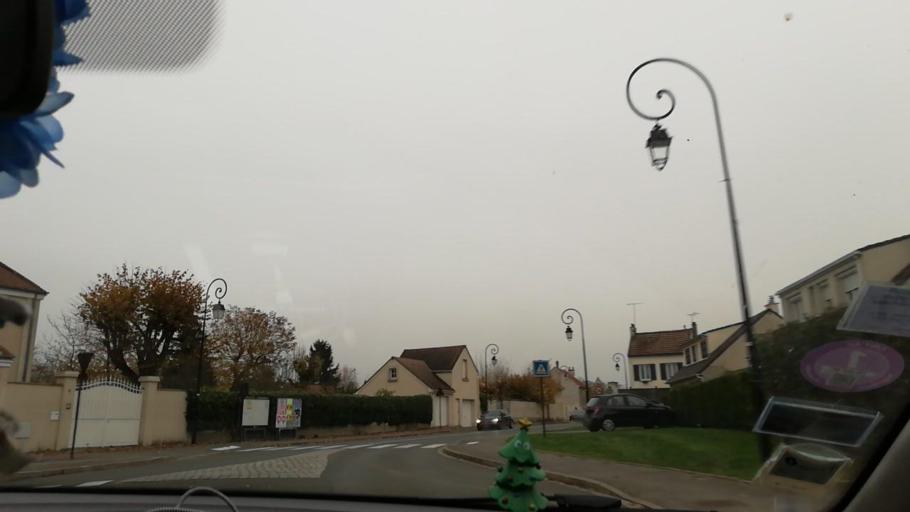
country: FR
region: Ile-de-France
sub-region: Departement de Seine-et-Marne
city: Claye-Souilly
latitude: 48.9495
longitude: 2.6765
